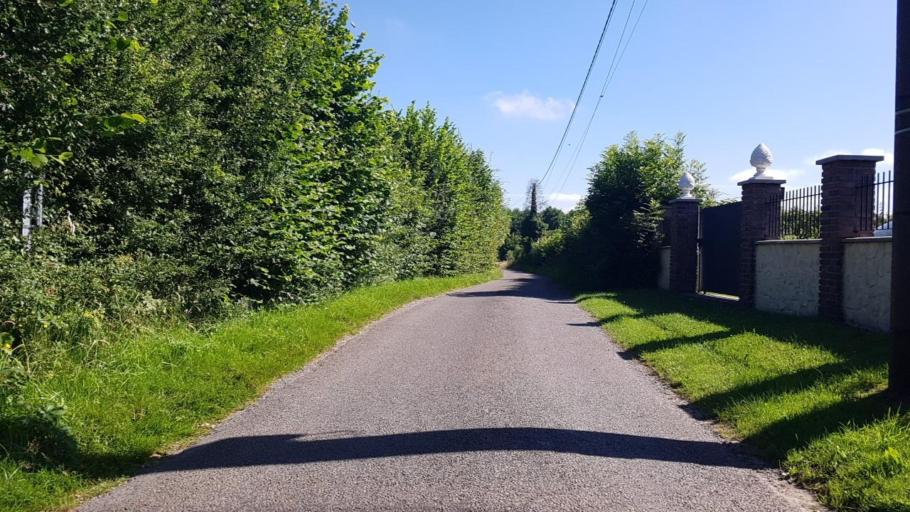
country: FR
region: Nord-Pas-de-Calais
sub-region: Departement du Nord
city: Anor
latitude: 49.9961
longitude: 4.1346
